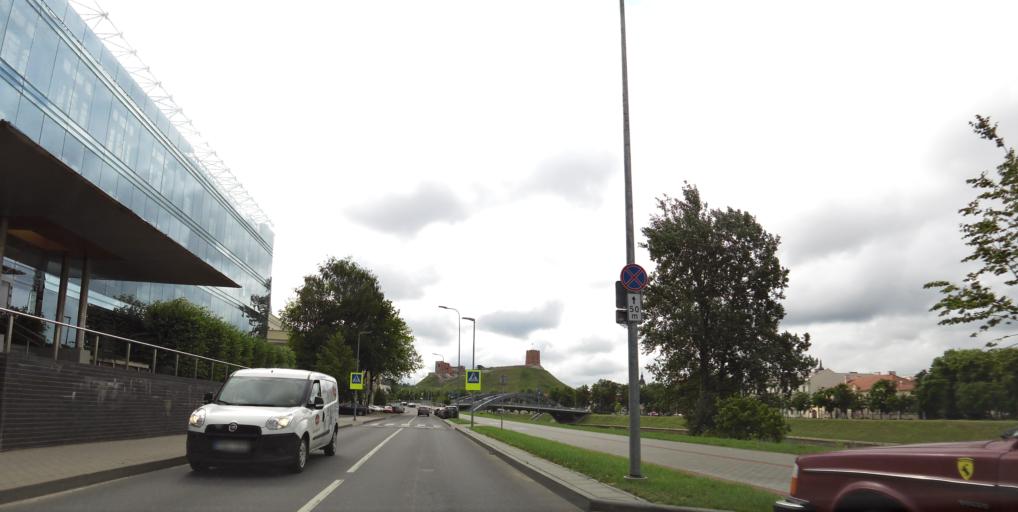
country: LT
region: Vilnius County
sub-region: Vilnius
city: Vilnius
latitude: 54.6908
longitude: 25.2861
